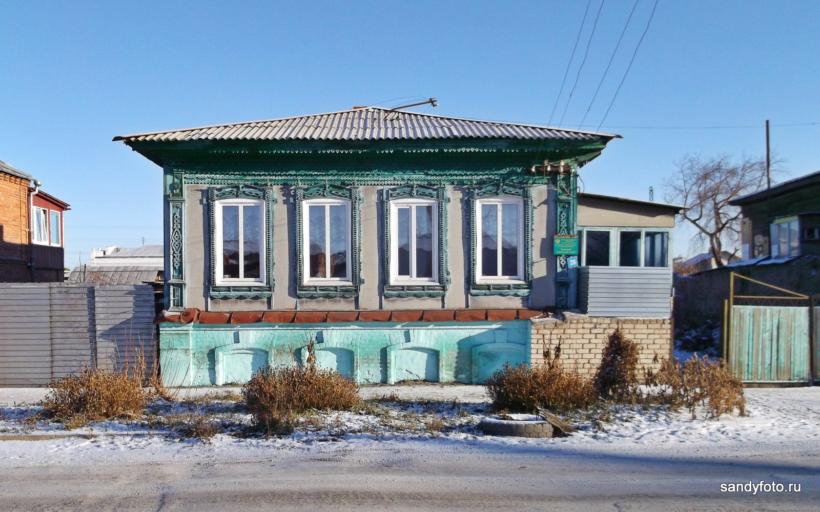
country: RU
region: Chelyabinsk
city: Troitsk
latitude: 54.0858
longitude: 61.5610
